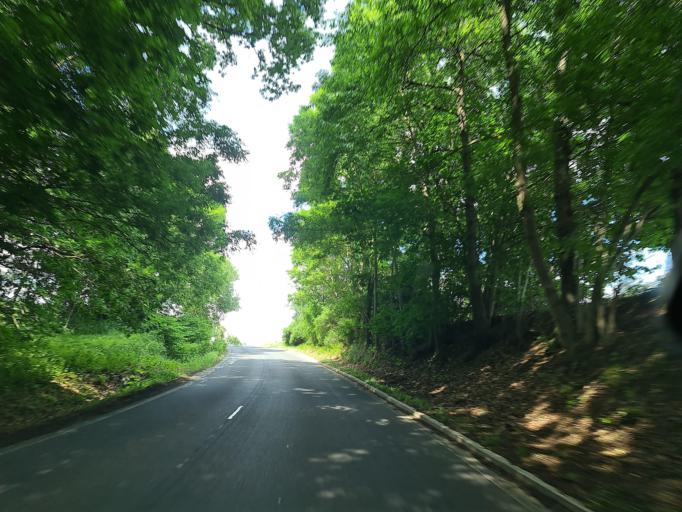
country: DE
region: Saxony
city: Syrau
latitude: 50.5143
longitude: 12.0922
